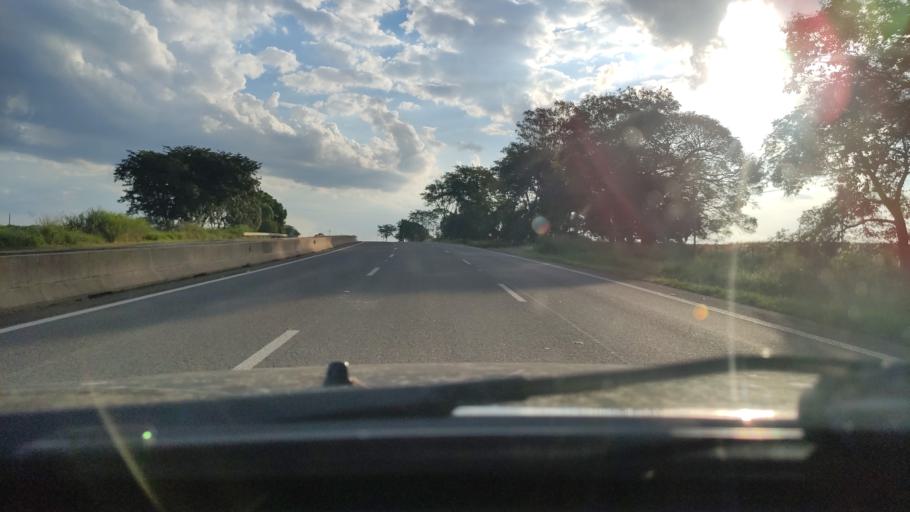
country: BR
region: Sao Paulo
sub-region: Mogi-Mirim
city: Mogi Mirim
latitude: -22.4508
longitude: -47.0832
